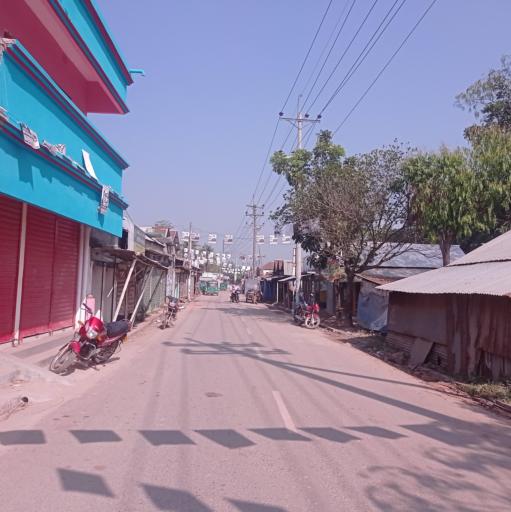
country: BD
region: Dhaka
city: Narsingdi
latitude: 24.0828
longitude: 90.6949
